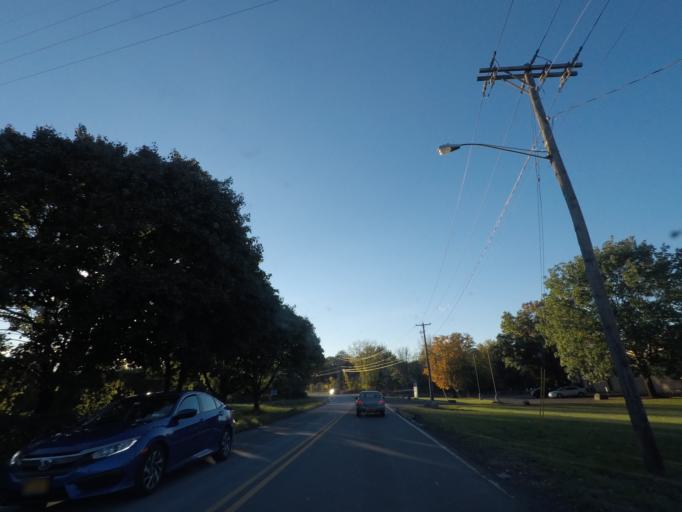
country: US
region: New York
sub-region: Albany County
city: Green Island
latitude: 42.7470
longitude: -73.7038
